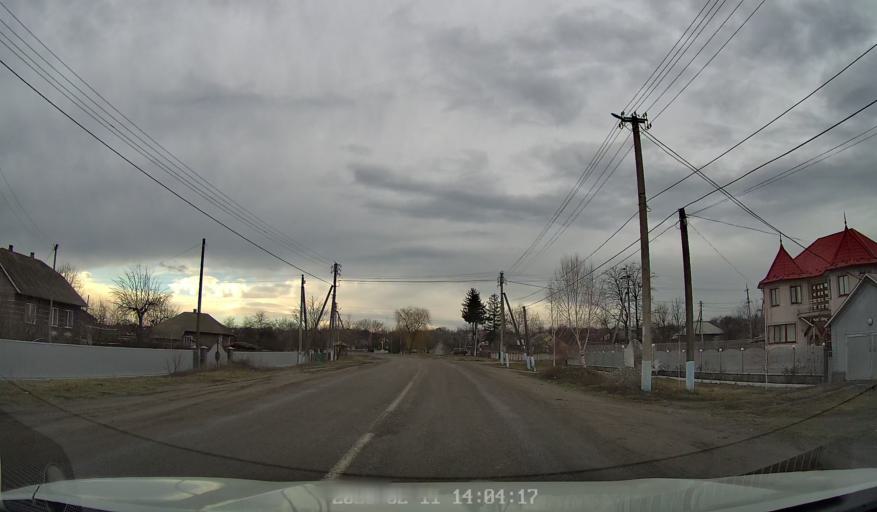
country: RO
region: Botosani
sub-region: Comuna Darabani
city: Bajura
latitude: 48.2589
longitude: 26.5875
